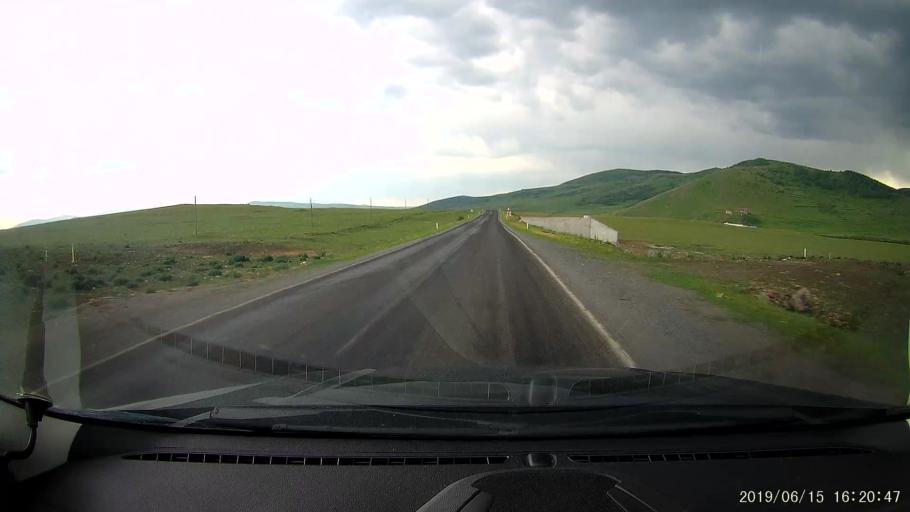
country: TR
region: Ardahan
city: Hanak
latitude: 41.2084
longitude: 42.8465
